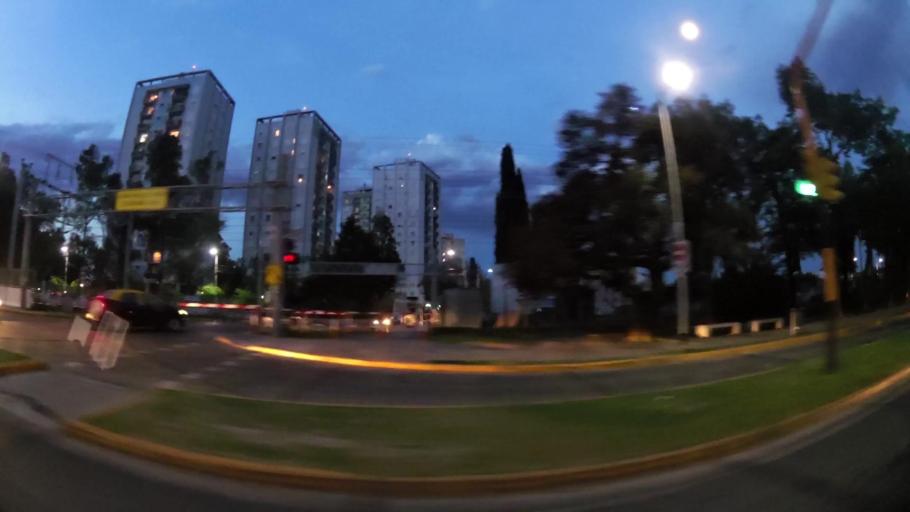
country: AR
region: Buenos Aires
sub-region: Partido de Avellaneda
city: Avellaneda
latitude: -34.6970
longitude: -58.3139
